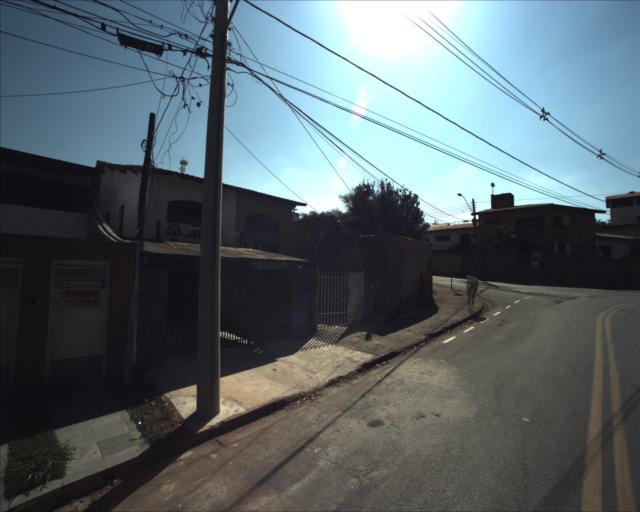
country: BR
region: Sao Paulo
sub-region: Sorocaba
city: Sorocaba
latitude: -23.4716
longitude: -47.4339
